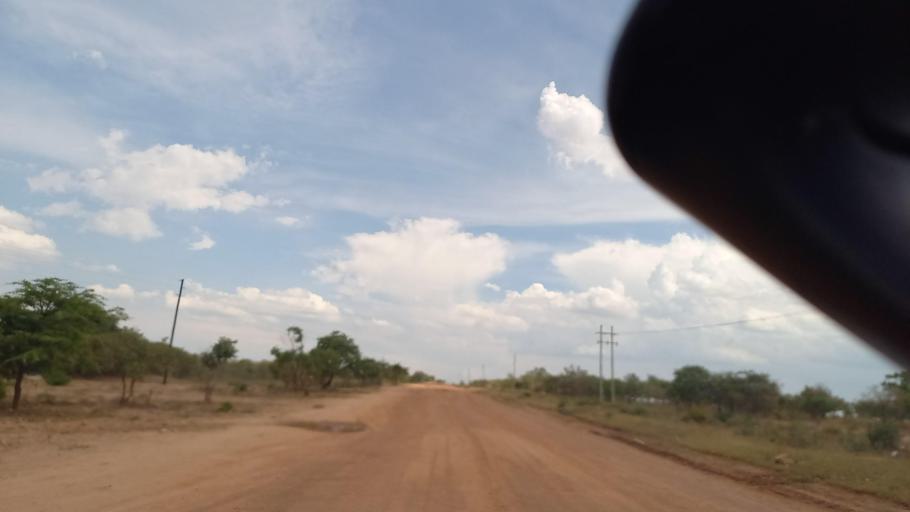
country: ZM
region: Lusaka
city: Kafue
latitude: -16.1419
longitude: 28.0538
